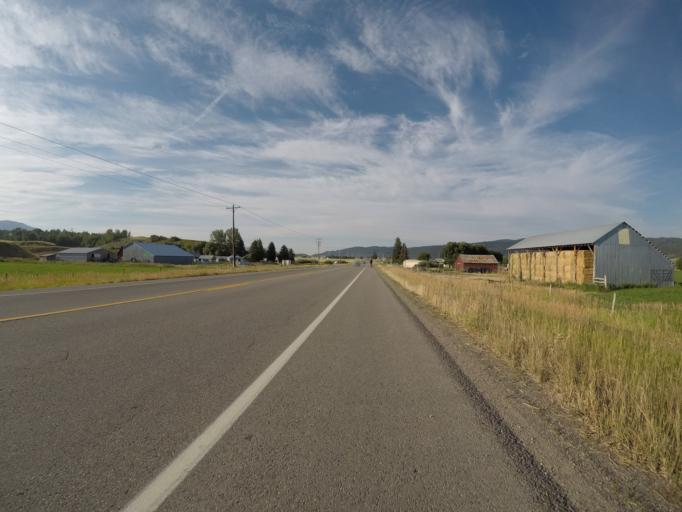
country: US
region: Wyoming
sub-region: Lincoln County
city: Afton
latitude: 42.9374
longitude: -111.0074
